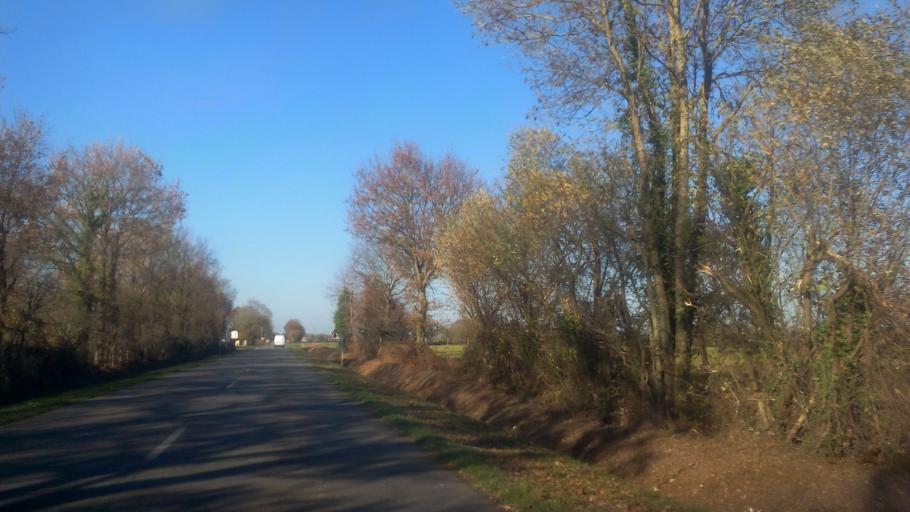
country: FR
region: Brittany
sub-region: Departement du Morbihan
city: Saint-Vincent-sur-Oust
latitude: 47.7099
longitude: -2.1703
